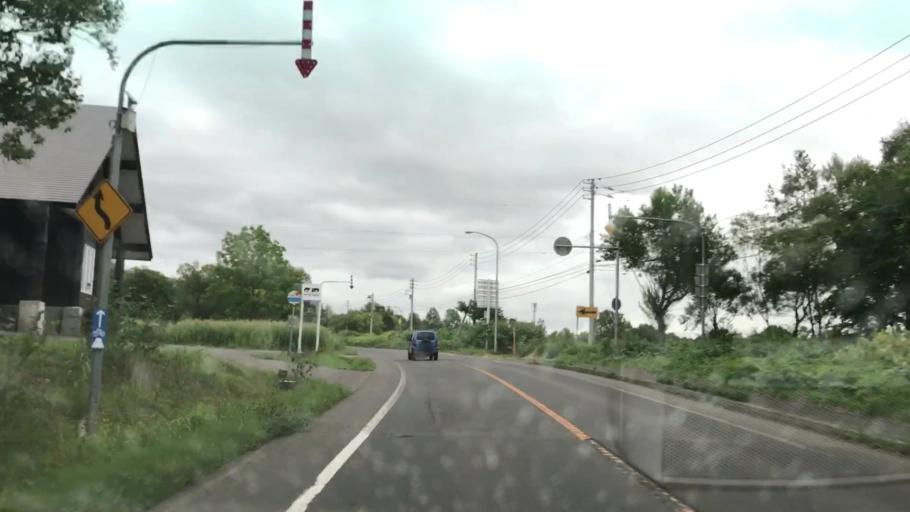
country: JP
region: Hokkaido
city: Niseko Town
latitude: 42.7950
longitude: 140.7530
